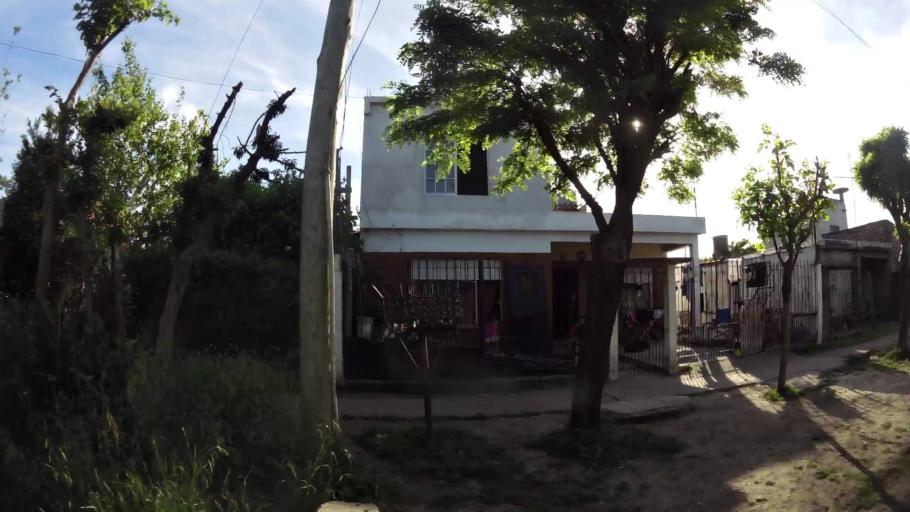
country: AR
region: Buenos Aires
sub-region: Partido de Almirante Brown
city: Adrogue
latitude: -34.8175
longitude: -58.3216
